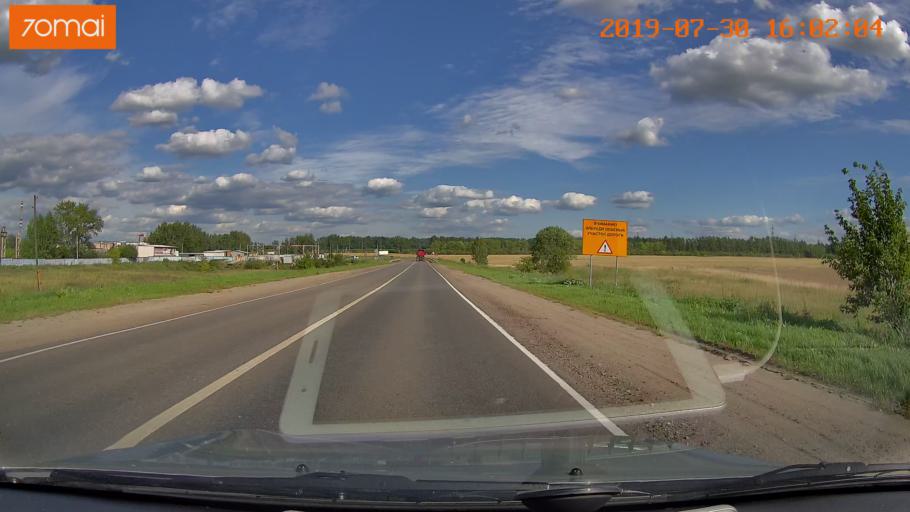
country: RU
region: Moskovskaya
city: Voskresensk
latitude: 55.2882
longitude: 38.6829
